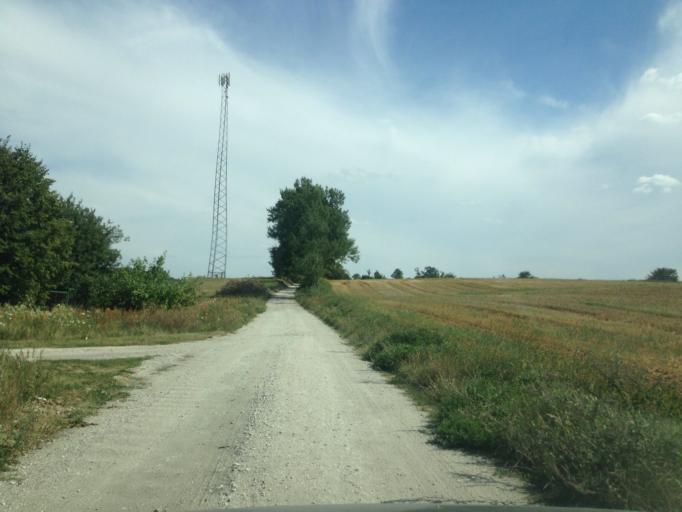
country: PL
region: Kujawsko-Pomorskie
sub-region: Powiat brodnicki
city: Gorzno
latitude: 53.2010
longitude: 19.6329
